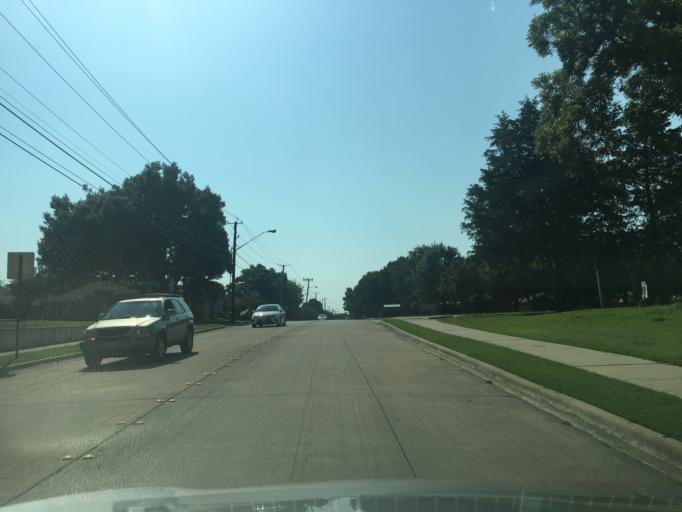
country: US
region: Texas
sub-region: Dallas County
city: Garland
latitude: 32.9450
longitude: -96.6368
